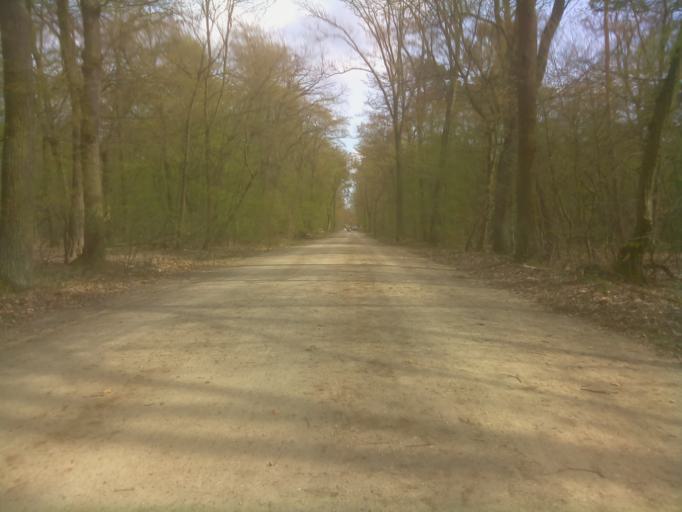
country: DE
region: Baden-Wuerttemberg
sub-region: Karlsruhe Region
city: Mannheim
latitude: 49.5404
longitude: 8.4926
